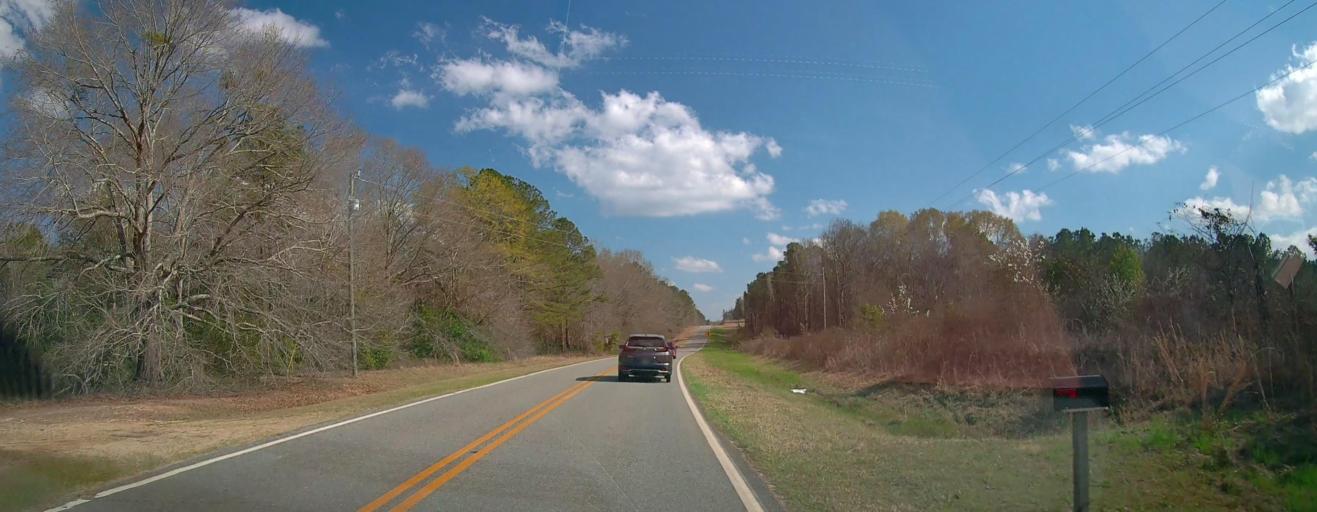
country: US
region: Georgia
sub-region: Wilkinson County
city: Irwinton
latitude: 32.6260
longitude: -83.0932
